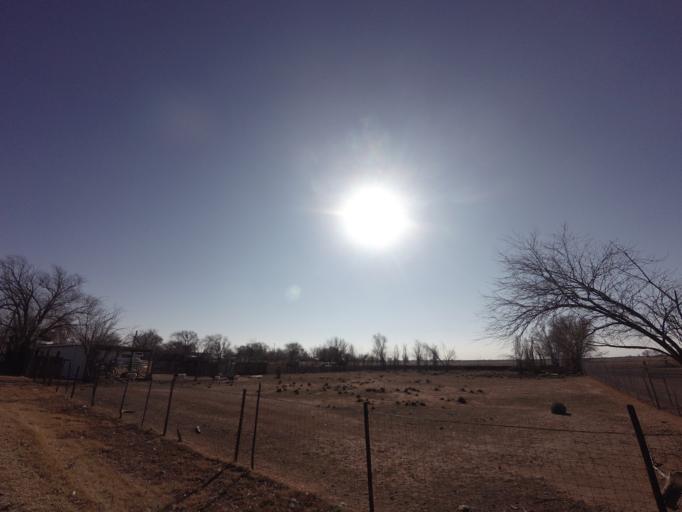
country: US
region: New Mexico
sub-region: Curry County
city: Clovis
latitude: 34.3864
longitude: -103.1861
